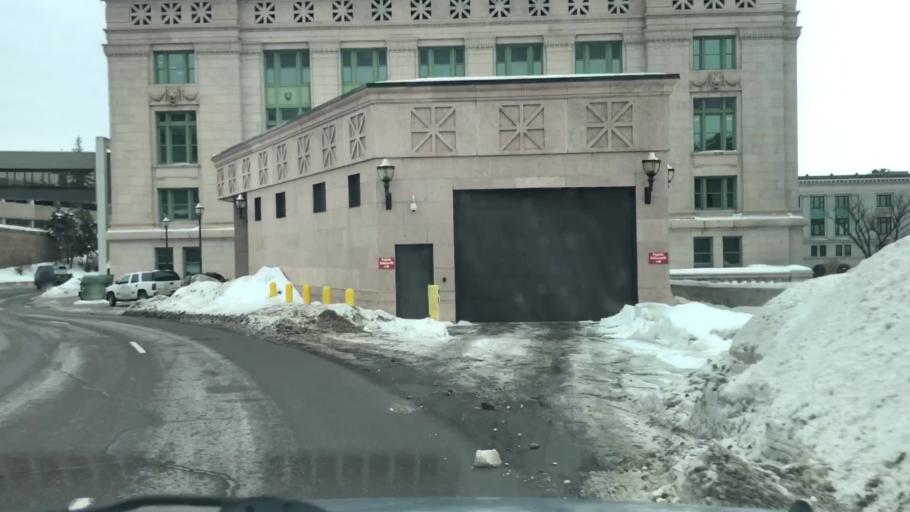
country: US
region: Minnesota
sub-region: Saint Louis County
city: Duluth
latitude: 46.7830
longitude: -92.1073
